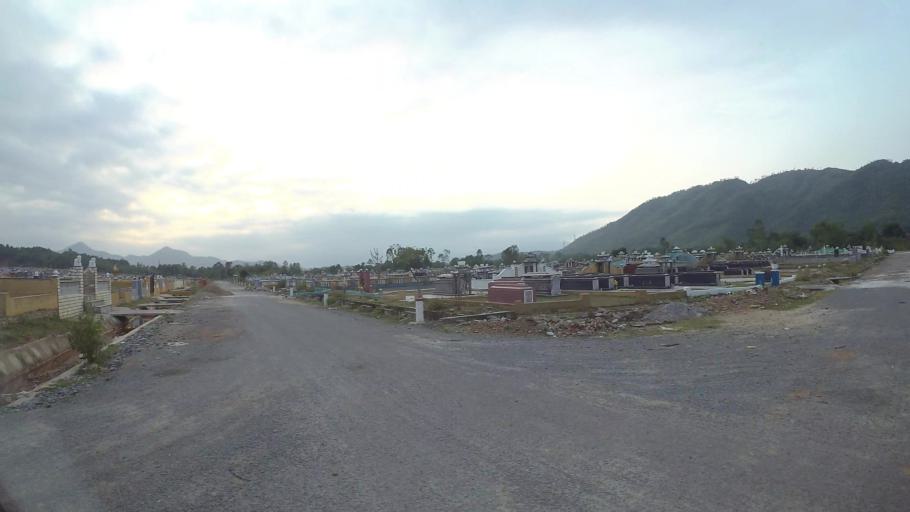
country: VN
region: Da Nang
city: Lien Chieu
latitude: 16.0560
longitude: 108.1232
